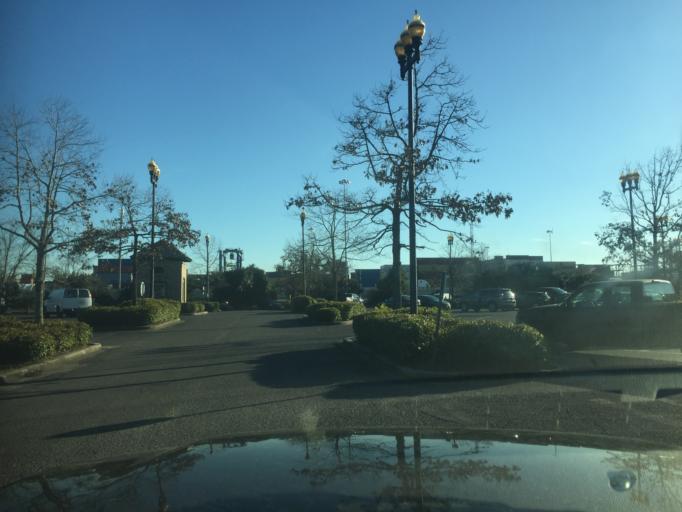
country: US
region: Louisiana
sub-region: Jefferson Parish
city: Marrero
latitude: 29.9170
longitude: -90.1019
